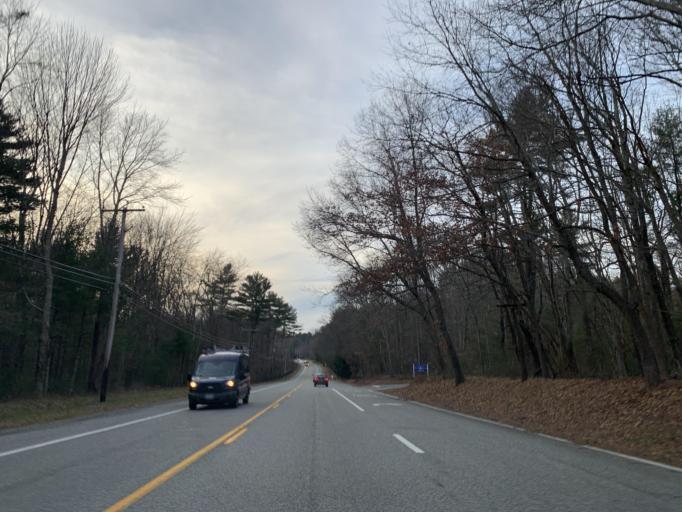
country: US
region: Rhode Island
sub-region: Providence County
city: Chepachet
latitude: 41.9194
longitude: -71.6898
